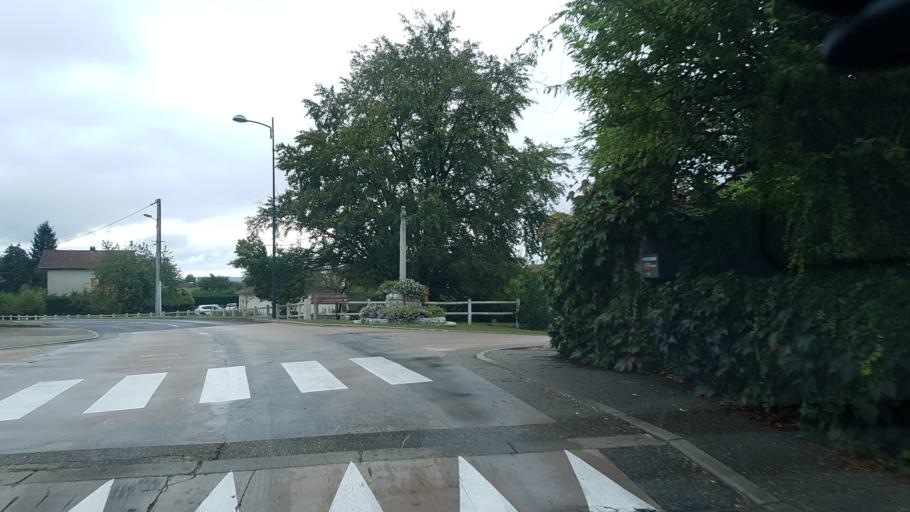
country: FR
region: Rhone-Alpes
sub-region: Departement de l'Ain
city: Tossiat
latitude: 46.1361
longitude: 5.3169
